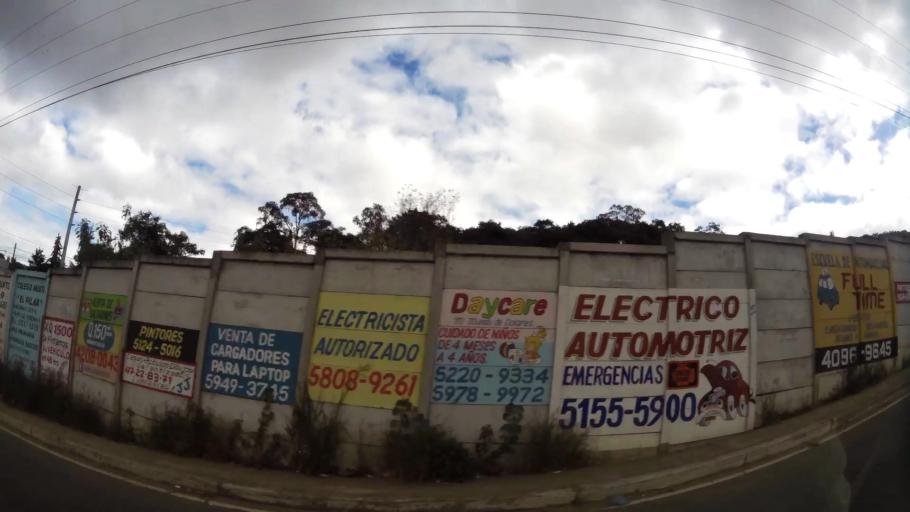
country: GT
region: Guatemala
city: Guatemala City
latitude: 14.6723
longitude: -90.5548
